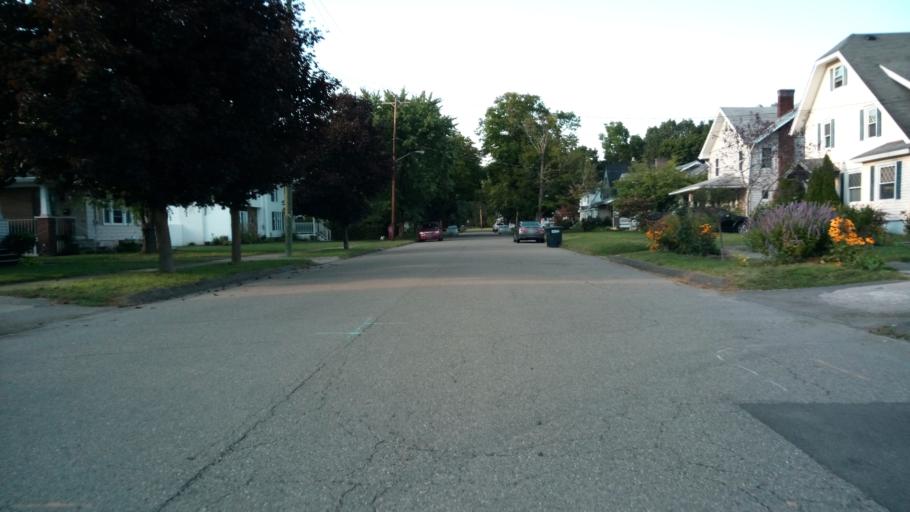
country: US
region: New York
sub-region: Chemung County
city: West Elmira
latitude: 42.0784
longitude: -76.8483
